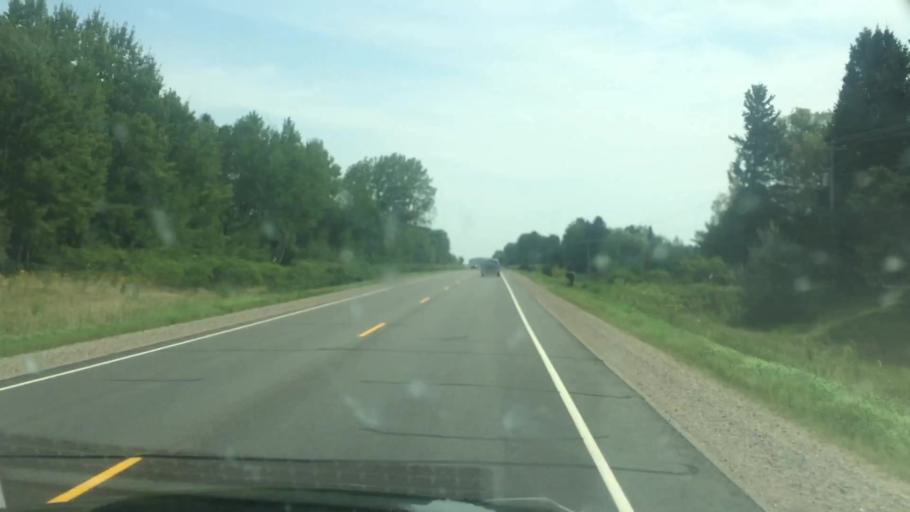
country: US
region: Wisconsin
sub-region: Langlade County
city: Antigo
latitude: 45.1681
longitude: -88.9349
